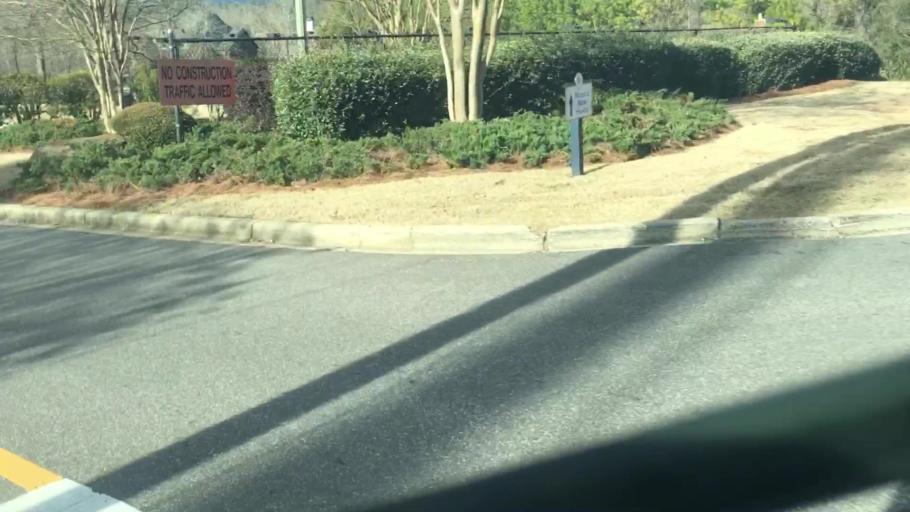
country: US
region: Alabama
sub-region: Shelby County
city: Brook Highland
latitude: 33.4792
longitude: -86.6688
